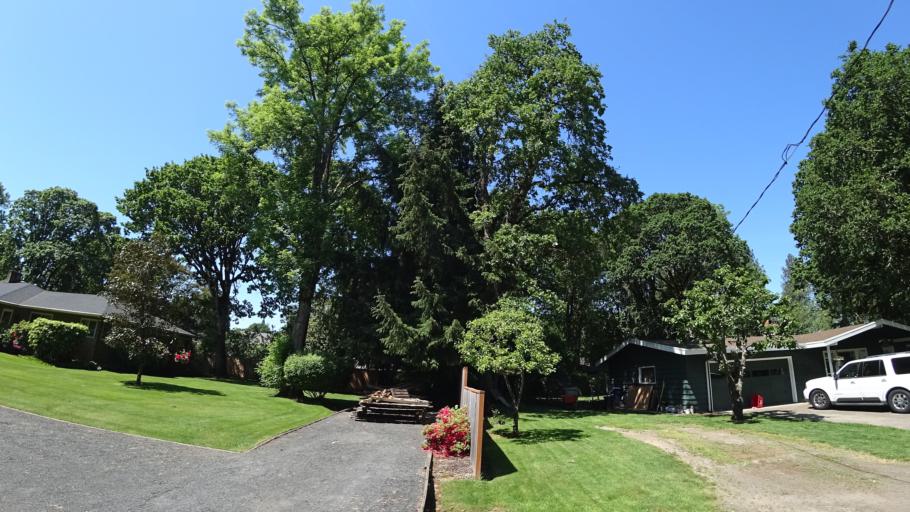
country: US
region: Oregon
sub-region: Washington County
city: Aloha
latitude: 45.4948
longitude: -122.8542
